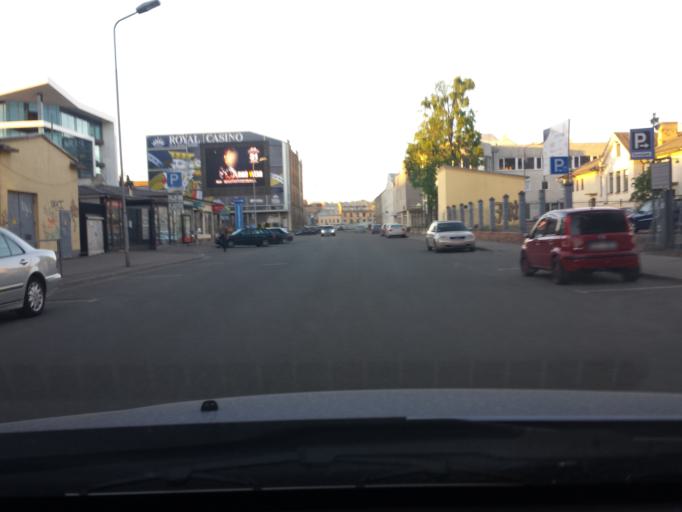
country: LV
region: Riga
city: Riga
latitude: 56.9584
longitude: 24.1319
